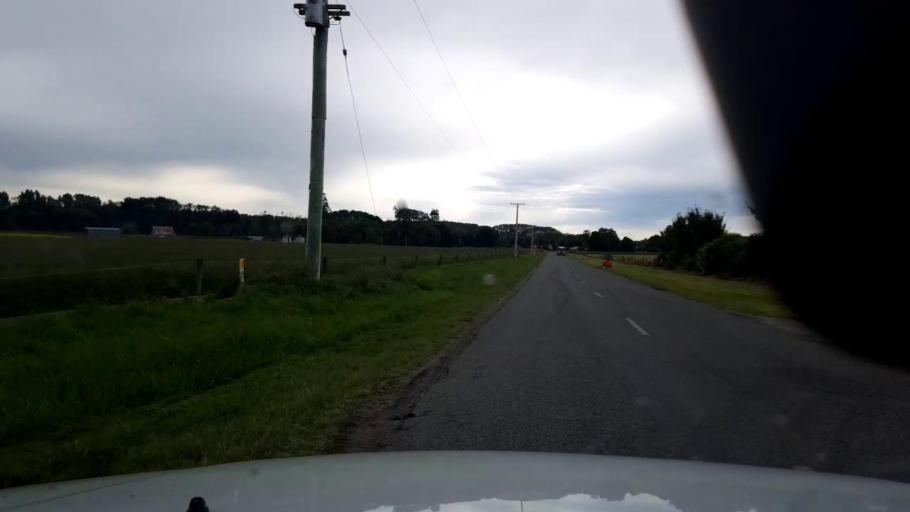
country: NZ
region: Canterbury
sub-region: Timaru District
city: Pleasant Point
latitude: -44.2698
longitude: 171.2588
